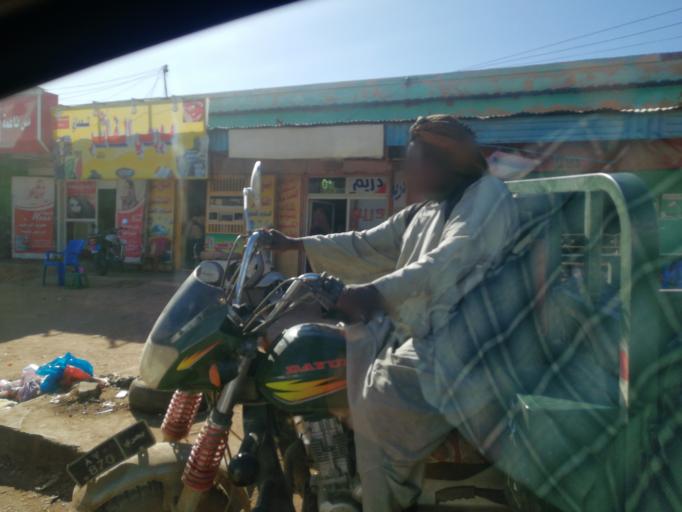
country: SD
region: Khartoum
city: Khartoum
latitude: 15.6108
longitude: 32.6201
